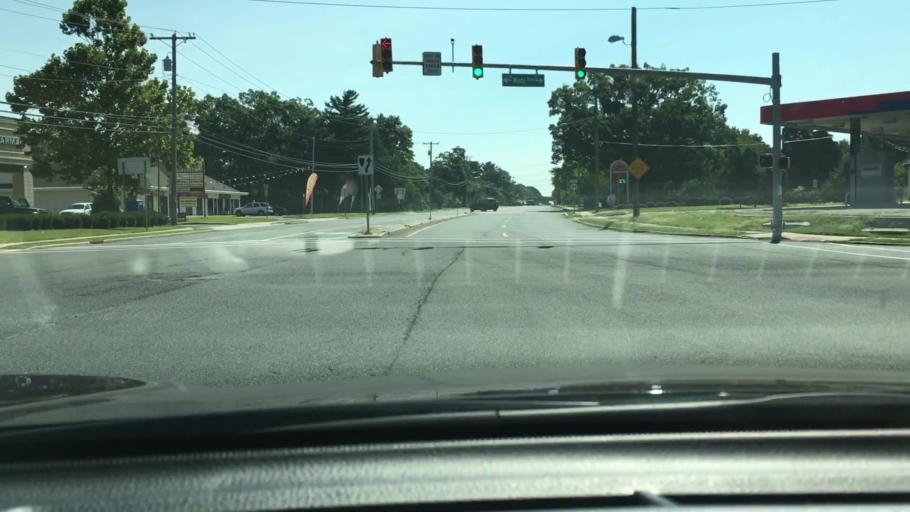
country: US
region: New Jersey
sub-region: Cumberland County
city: Millville
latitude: 39.3947
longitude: -75.0184
